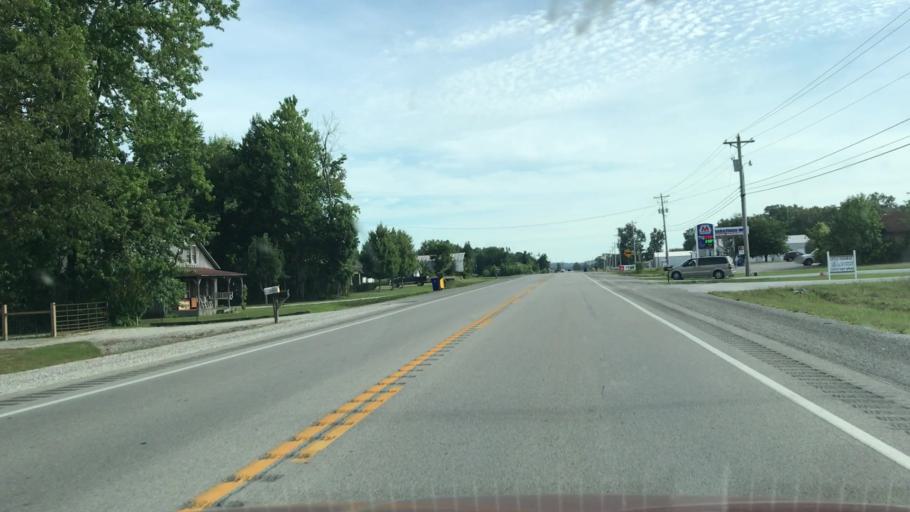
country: US
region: Kentucky
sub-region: Edmonson County
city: Brownsville
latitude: 37.1300
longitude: -86.2346
